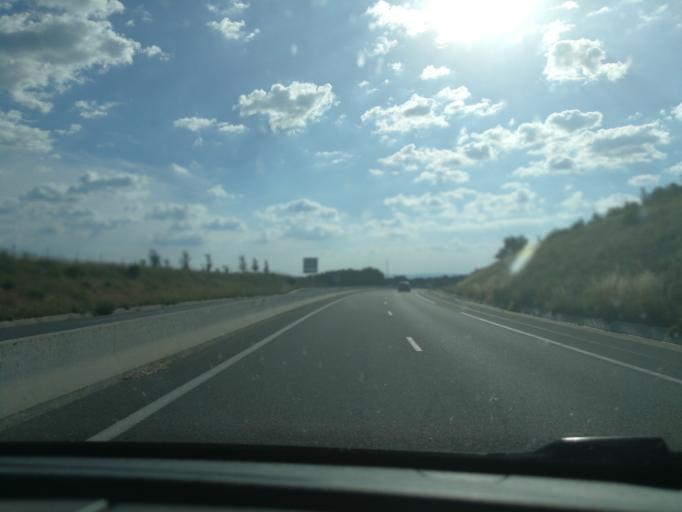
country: FR
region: Midi-Pyrenees
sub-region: Departement du Tarn
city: Carmaux
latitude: 44.0787
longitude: 2.2560
